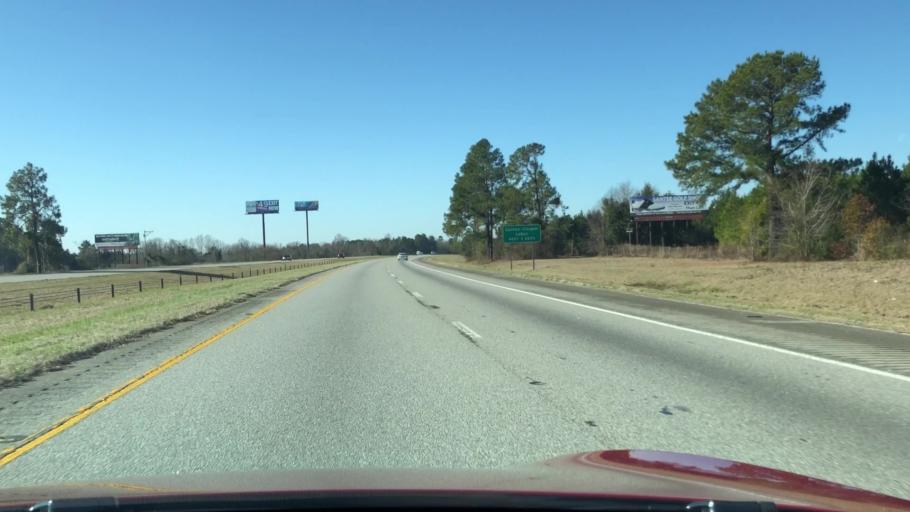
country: US
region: South Carolina
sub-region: Clarendon County
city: Manning
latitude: 33.6013
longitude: -80.3268
